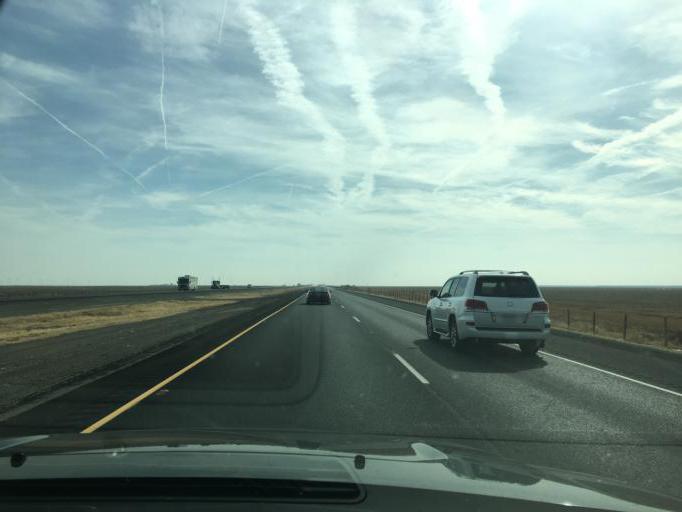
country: US
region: California
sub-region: Kern County
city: Lost Hills
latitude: 35.6938
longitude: -119.7111
